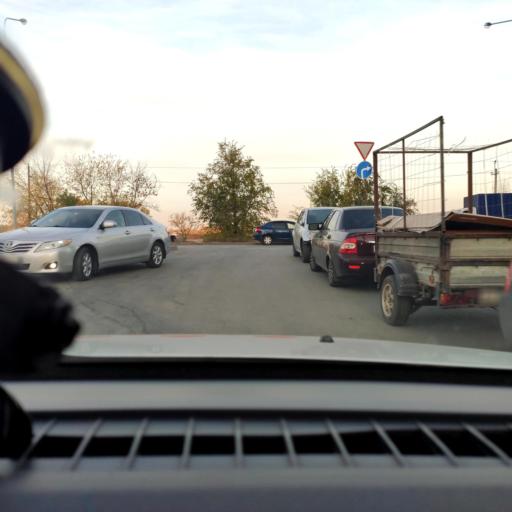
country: RU
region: Samara
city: Samara
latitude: 53.1086
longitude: 50.1375
